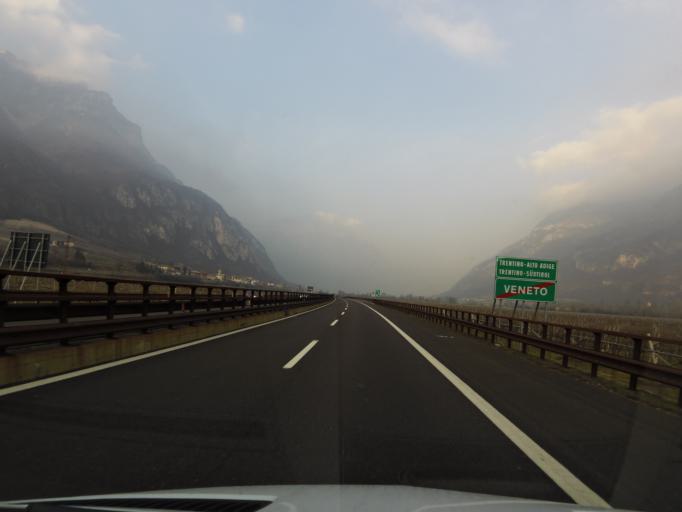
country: IT
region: Trentino-Alto Adige
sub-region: Provincia di Trento
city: Avio
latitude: 45.6994
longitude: 10.9212
